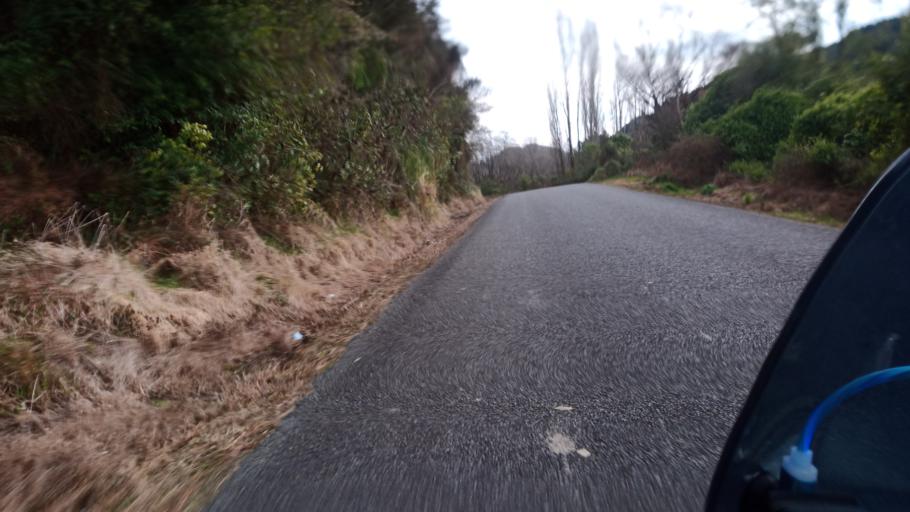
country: NZ
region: Hawke's Bay
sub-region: Wairoa District
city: Wairoa
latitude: -38.8218
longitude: 177.4952
